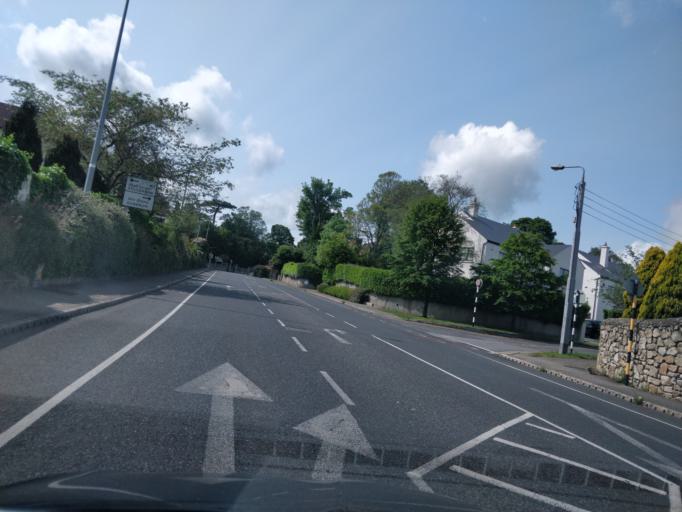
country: IE
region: Leinster
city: Balally
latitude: 53.2906
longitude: -6.2340
